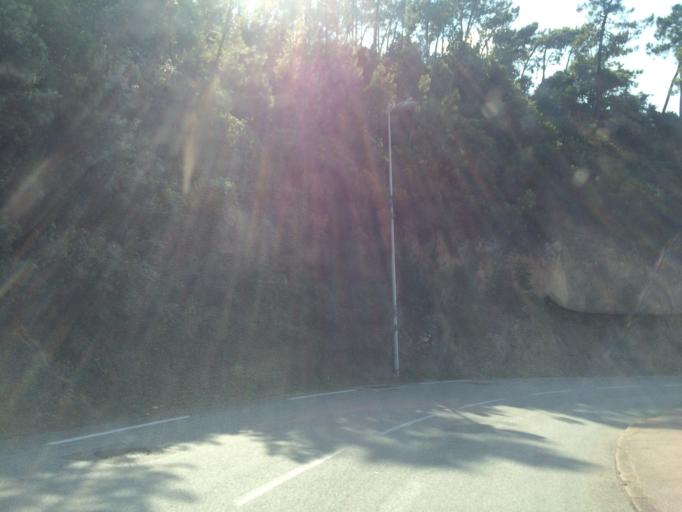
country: FR
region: Provence-Alpes-Cote d'Azur
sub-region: Departement des Alpes-Maritimes
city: Theoule-sur-Mer
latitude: 43.5047
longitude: 6.9492
